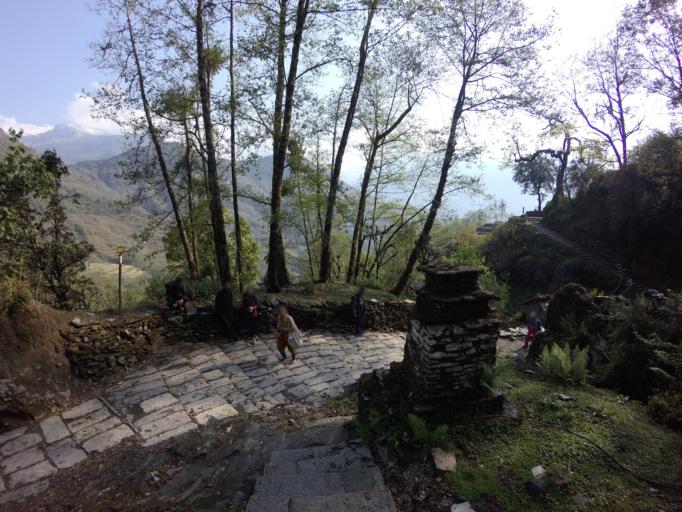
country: NP
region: Western Region
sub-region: Dhawalagiri Zone
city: Chitre
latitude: 28.3816
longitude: 83.8024
